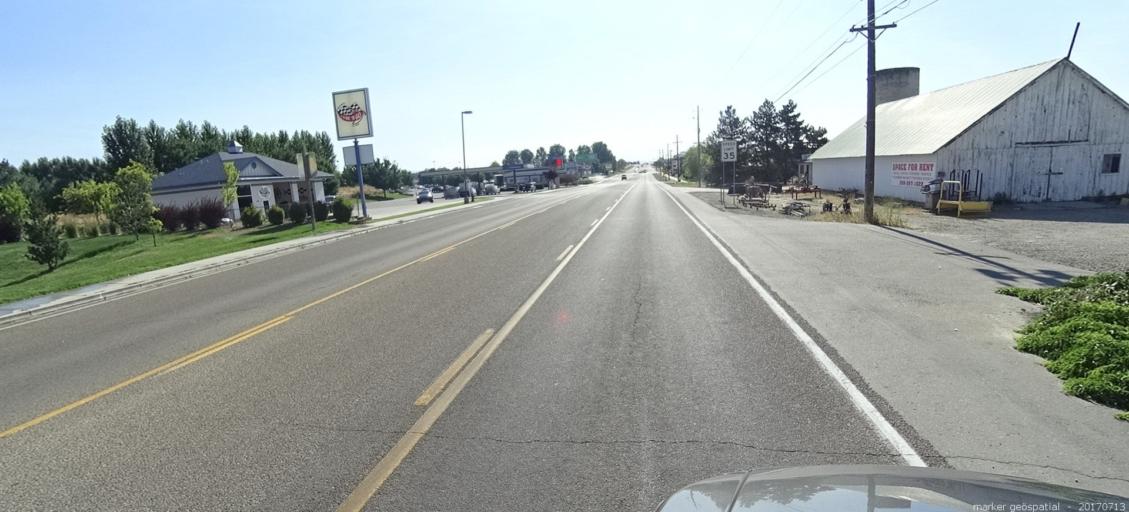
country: US
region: Idaho
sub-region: Ada County
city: Kuna
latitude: 43.4884
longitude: -116.4080
